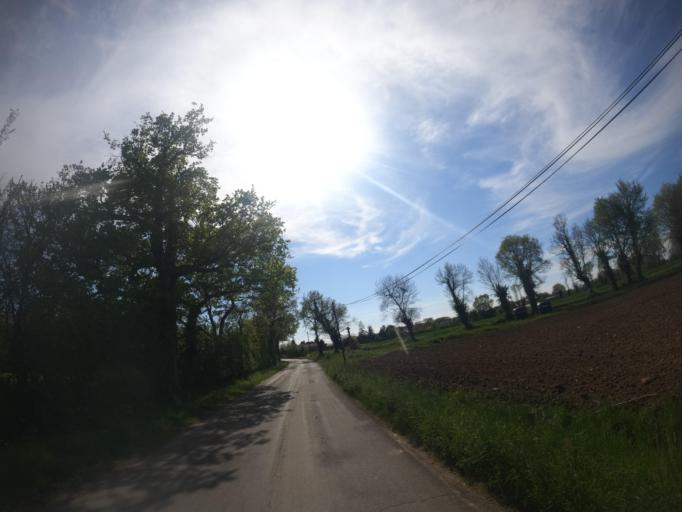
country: FR
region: Poitou-Charentes
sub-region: Departement des Deux-Sevres
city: Saint-Jean-de-Thouars
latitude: 46.9267
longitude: -0.2186
